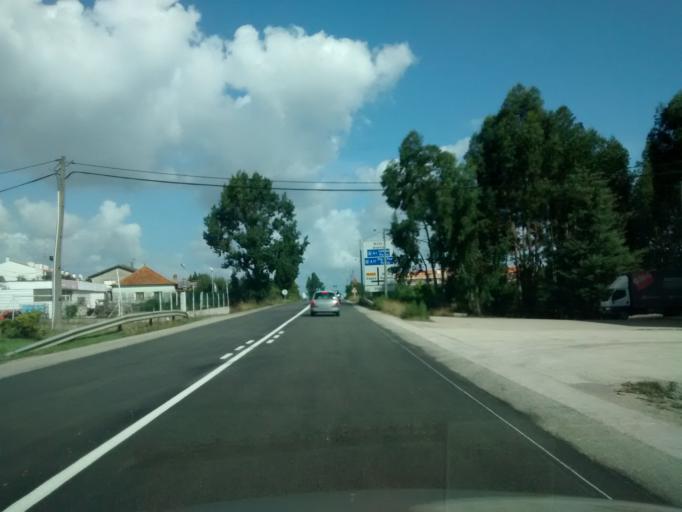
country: PT
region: Aveiro
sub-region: Oliveira do Bairro
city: Oia
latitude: 40.5411
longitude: -8.5312
